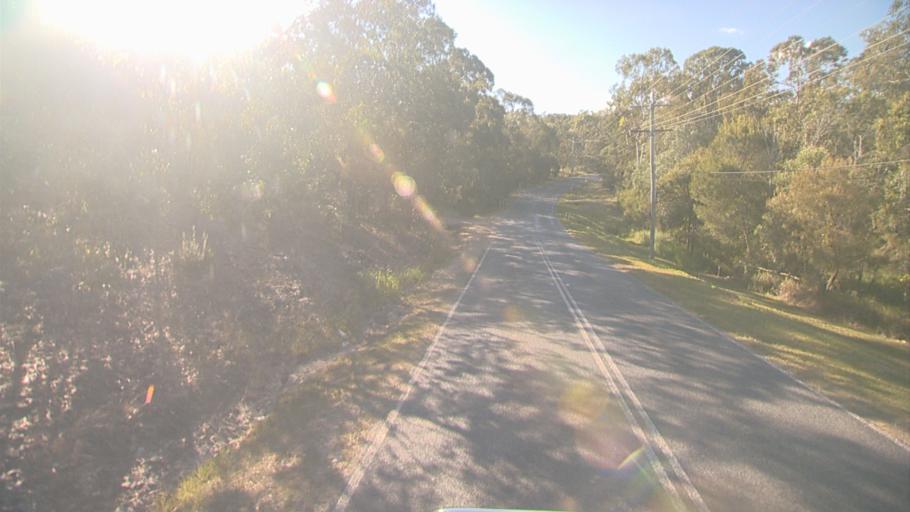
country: AU
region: Queensland
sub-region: Logan
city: Windaroo
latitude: -27.7295
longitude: 153.1716
